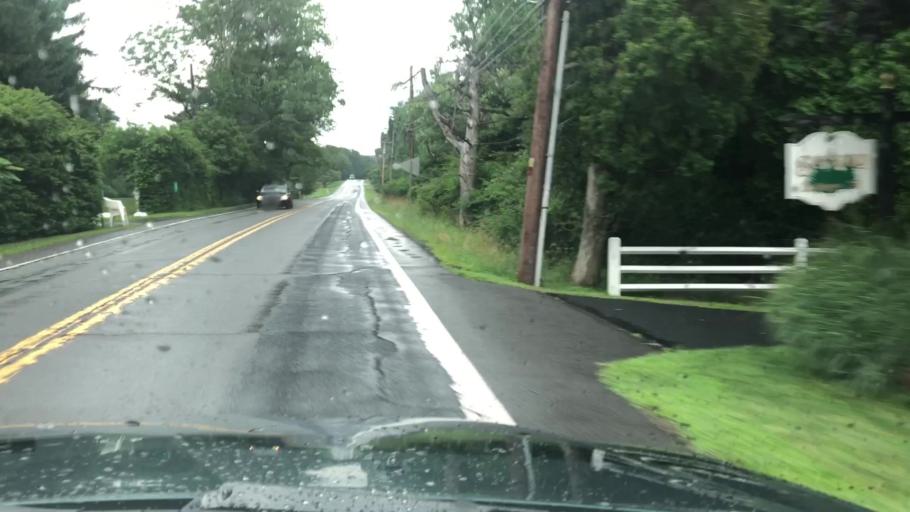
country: US
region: Pennsylvania
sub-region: Monroe County
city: Mountainhome
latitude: 41.2227
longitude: -75.2335
